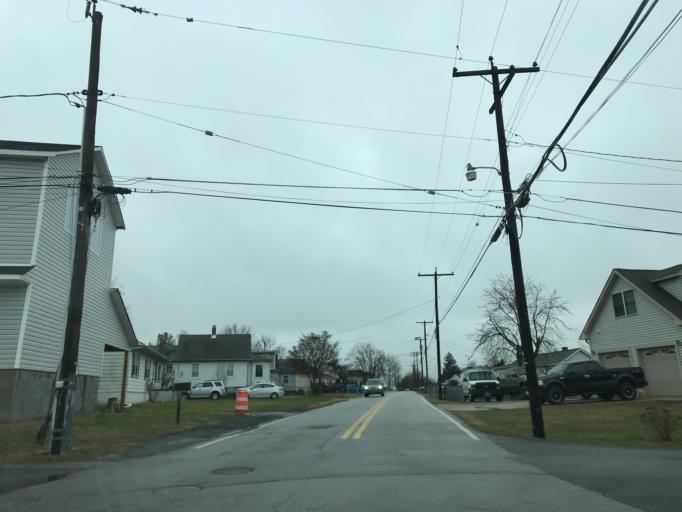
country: US
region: Maryland
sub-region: Baltimore County
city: Edgemere
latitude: 39.2228
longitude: -76.4521
